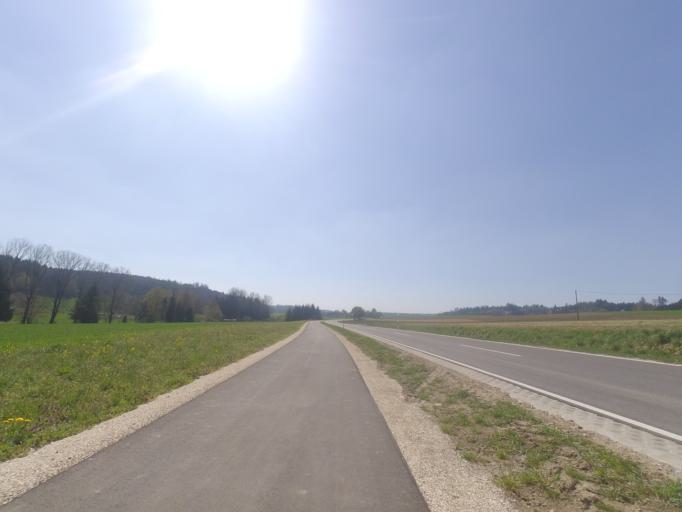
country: DE
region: Bavaria
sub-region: Swabia
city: Roggenburg
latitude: 48.3077
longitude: 10.2100
